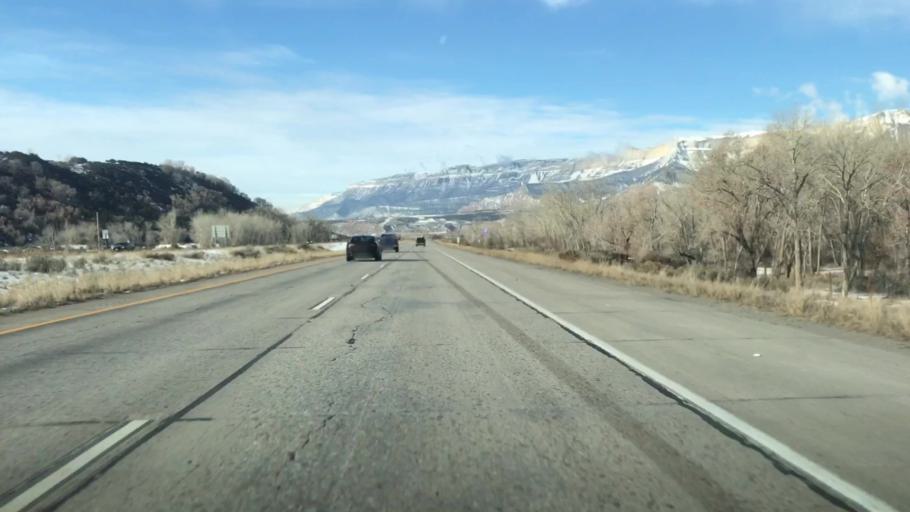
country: US
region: Colorado
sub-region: Garfield County
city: Rifle
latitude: 39.5203
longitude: -107.8021
